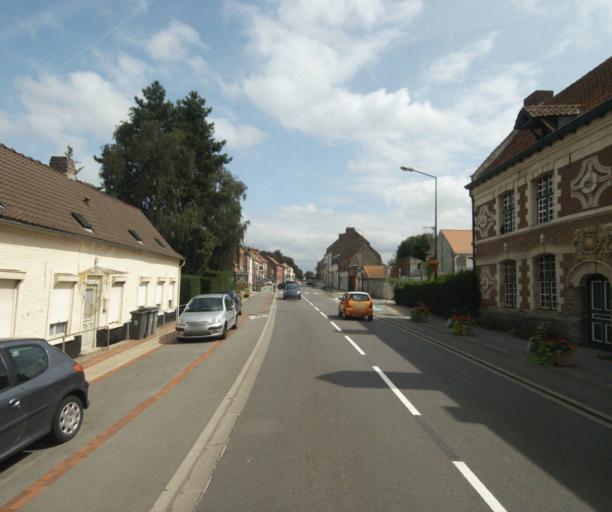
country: FR
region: Nord-Pas-de-Calais
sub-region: Departement du Nord
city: Tressin
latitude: 50.6115
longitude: 3.1965
